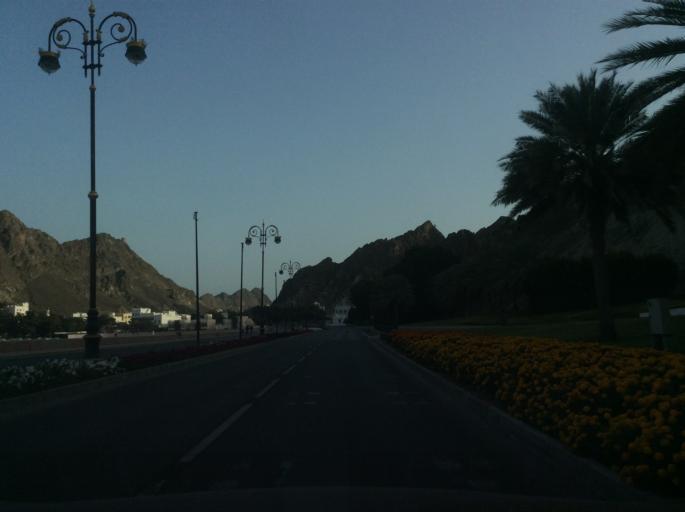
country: OM
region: Muhafazat Masqat
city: Muscat
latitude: 23.6236
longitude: 58.5810
